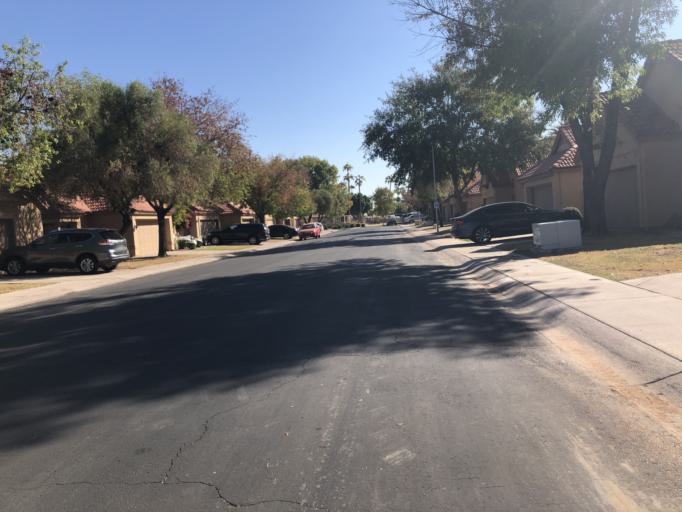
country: US
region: Arizona
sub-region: Maricopa County
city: Guadalupe
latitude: 33.3180
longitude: -111.9234
